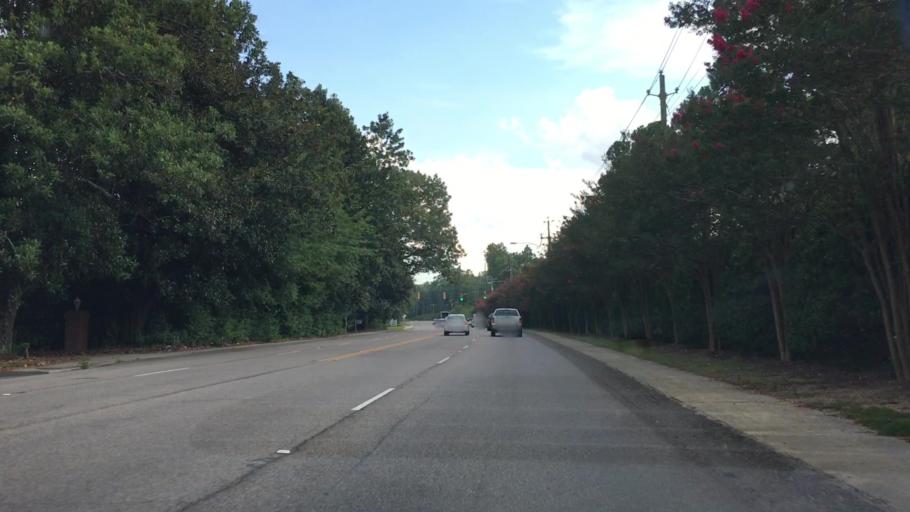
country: US
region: South Carolina
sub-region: Aiken County
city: Aiken
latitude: 33.5402
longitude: -81.7232
